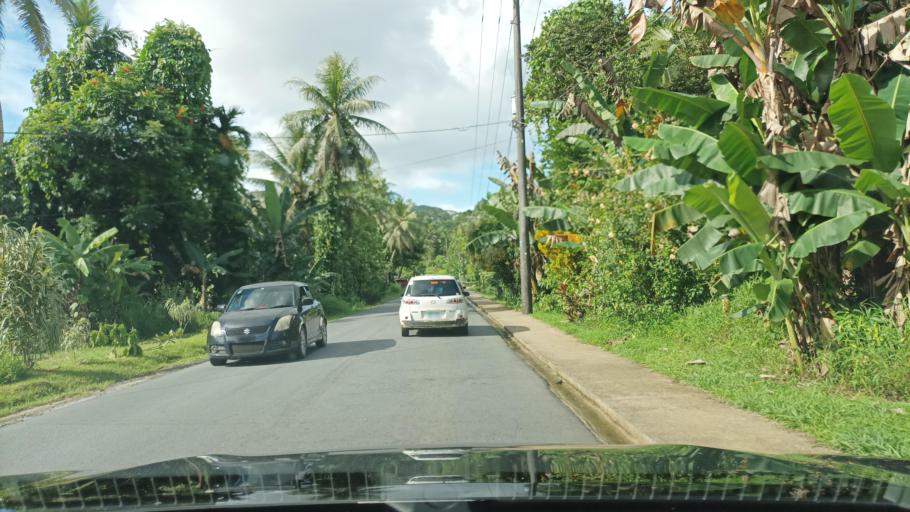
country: FM
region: Pohnpei
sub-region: Sokehs Municipality
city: Palikir - National Government Center
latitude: 6.9373
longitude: 158.1837
